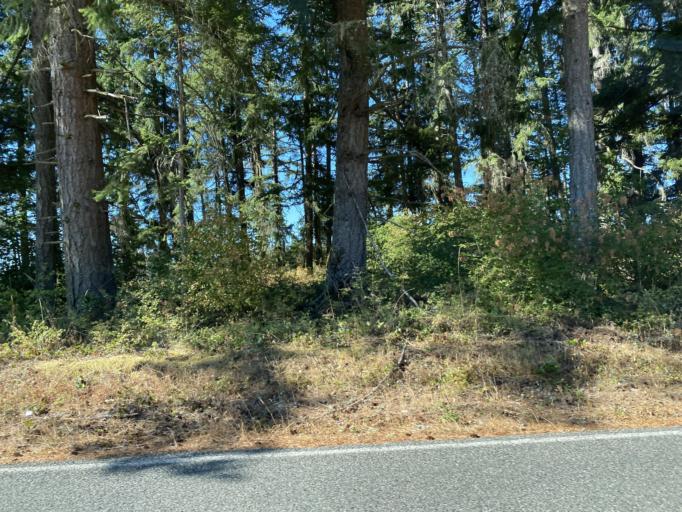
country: US
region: Washington
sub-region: Thurston County
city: Rainier
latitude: 46.9009
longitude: -122.7588
